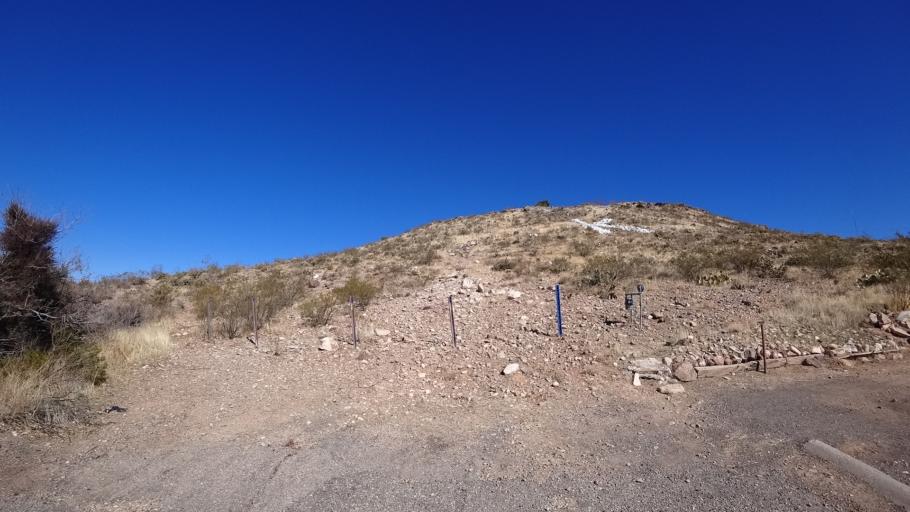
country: US
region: Arizona
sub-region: Mohave County
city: Kingman
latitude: 35.1955
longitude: -114.0553
